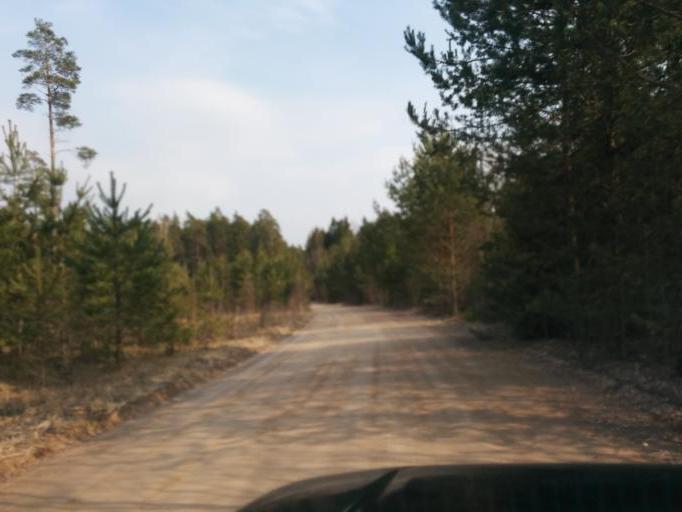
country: LV
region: Olaine
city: Olaine
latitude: 56.7890
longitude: 24.0441
